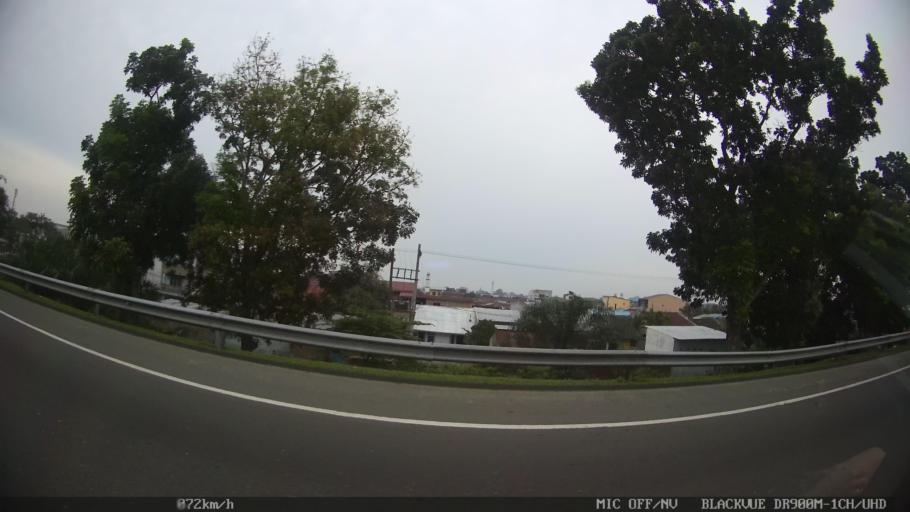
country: ID
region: North Sumatra
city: Medan
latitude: 3.5882
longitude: 98.7241
